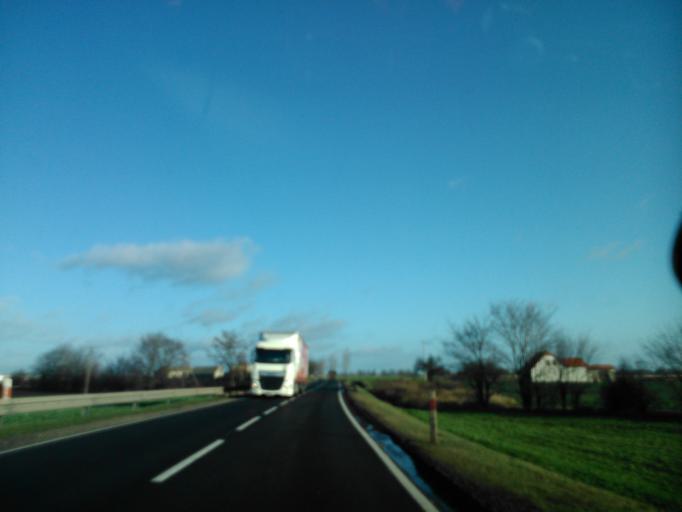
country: PL
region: Kujawsko-Pomorskie
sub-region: Powiat inowroclawski
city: Wierzchoslawice
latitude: 52.8584
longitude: 18.3515
